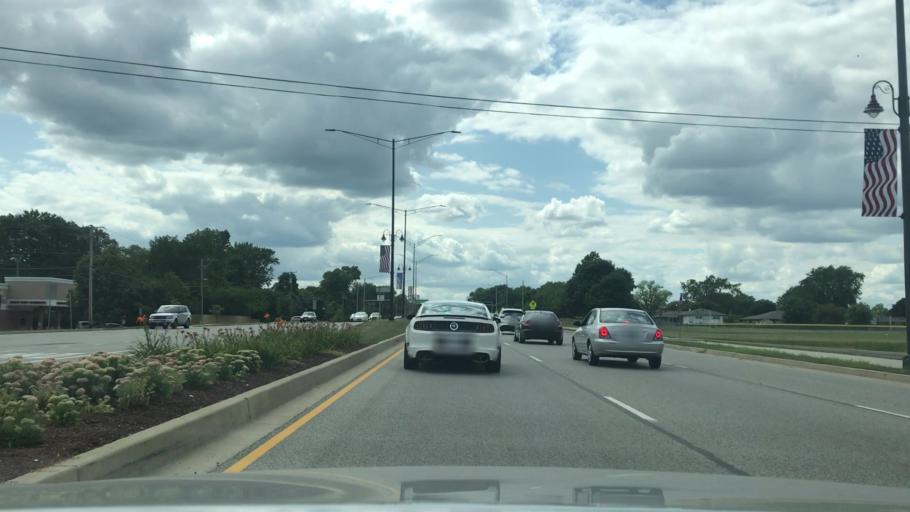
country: US
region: Illinois
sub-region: DuPage County
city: Darien
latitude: 41.7519
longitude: -87.9746
